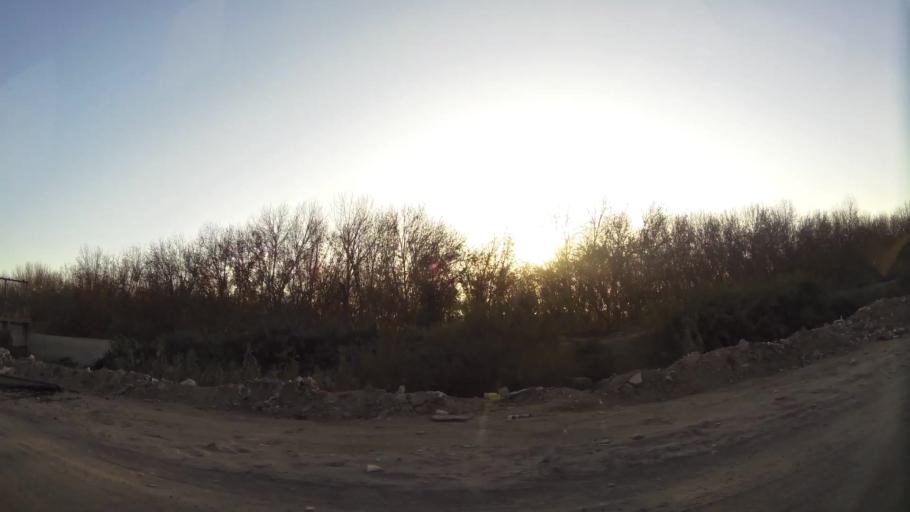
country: PE
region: Ica
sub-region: Provincia de Ica
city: Ica
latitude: -14.0878
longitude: -75.7180
